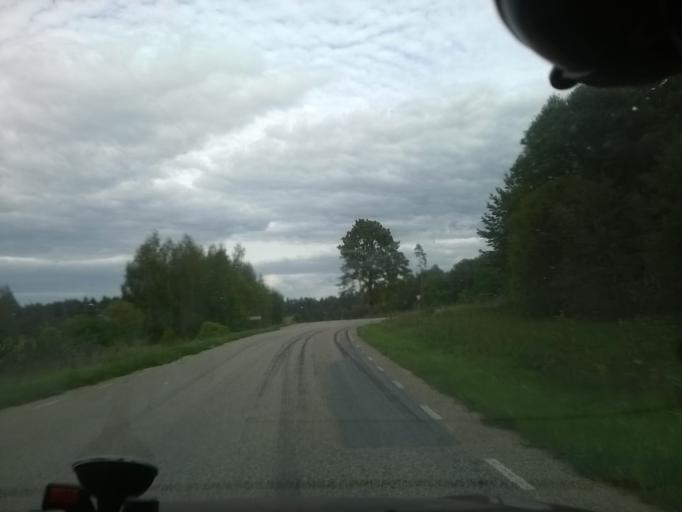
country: EE
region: Vorumaa
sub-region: Voru linn
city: Voru
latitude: 57.7507
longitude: 26.9730
